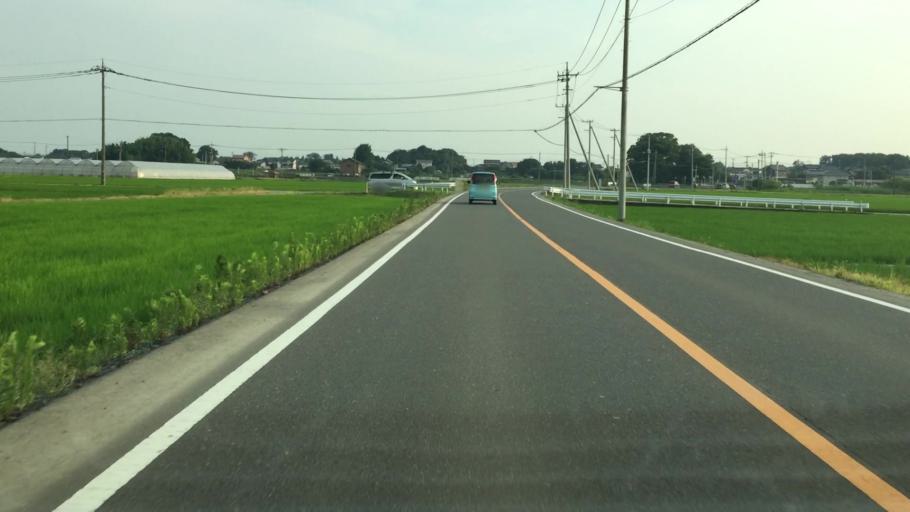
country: JP
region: Tochigi
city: Fujioka
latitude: 36.2395
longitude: 139.5934
